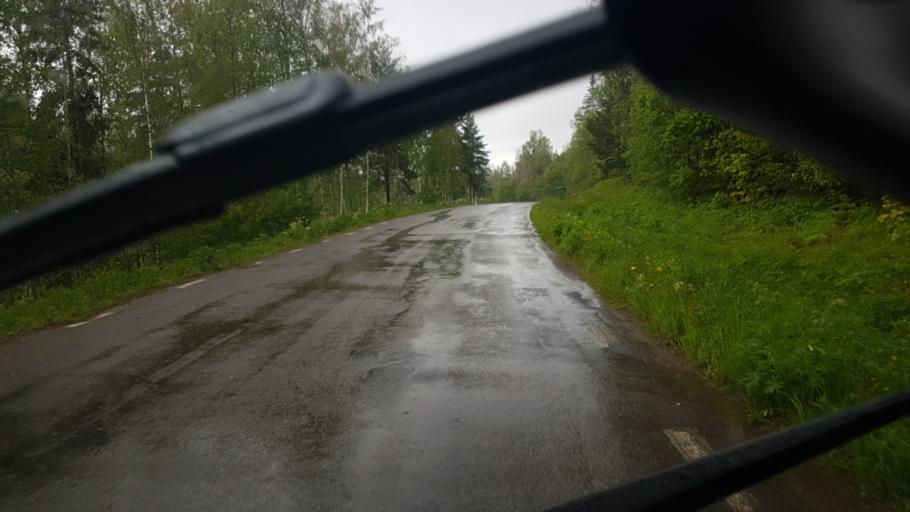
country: SE
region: Vaermland
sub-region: Eda Kommun
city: Amotfors
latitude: 59.7126
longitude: 12.4416
